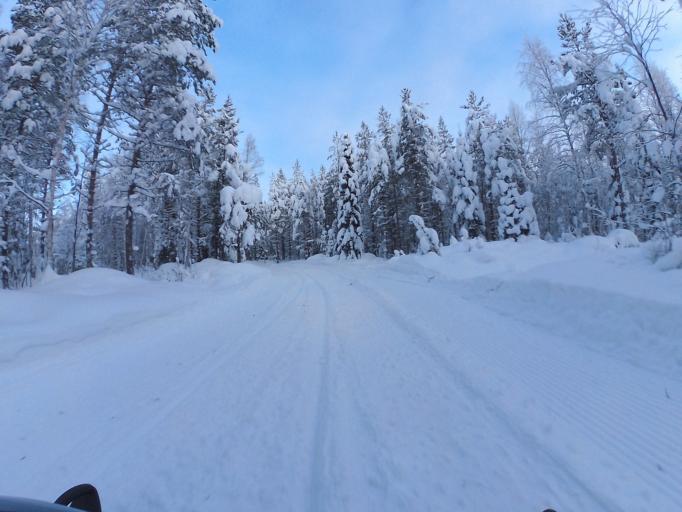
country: FI
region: Lapland
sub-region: Rovaniemi
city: Rovaniemi
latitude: 66.5302
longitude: 26.0363
